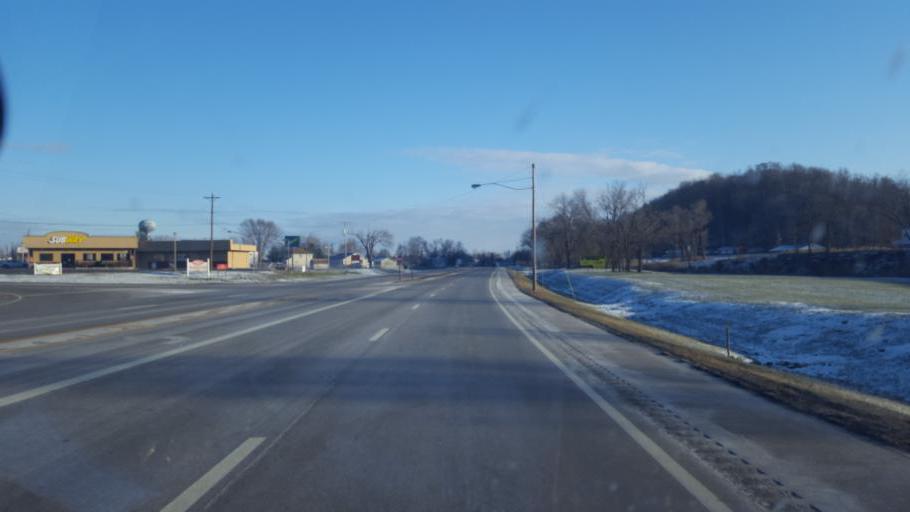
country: US
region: Ohio
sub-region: Pike County
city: Piketon
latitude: 39.0620
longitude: -83.0169
